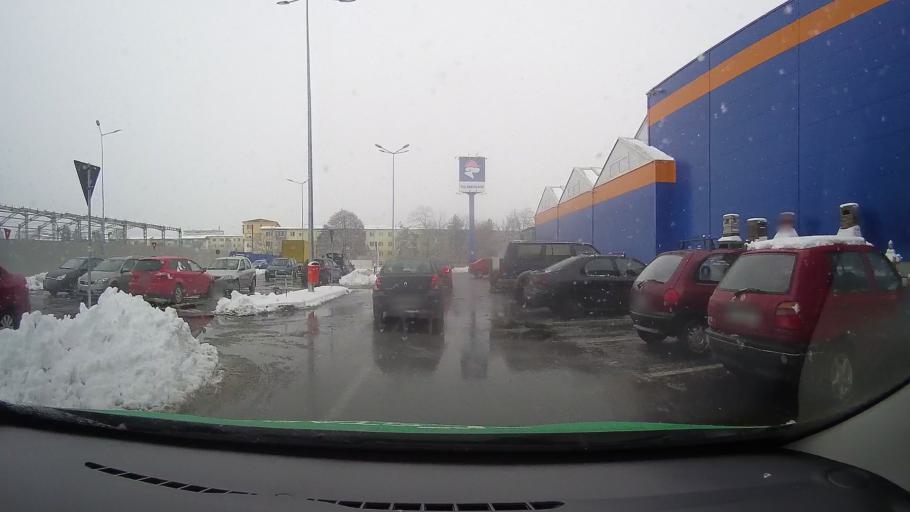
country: RO
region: Hunedoara
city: Hunedoara
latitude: 45.7666
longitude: 22.9041
